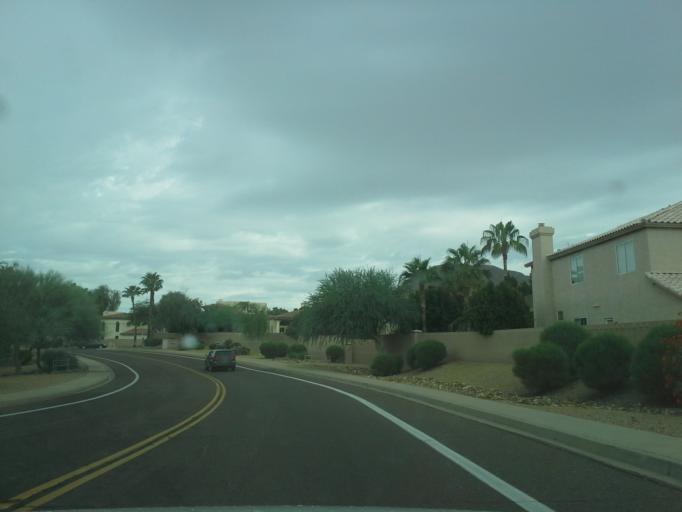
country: US
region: Arizona
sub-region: Maricopa County
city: Paradise Valley
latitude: 33.6162
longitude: -112.0474
